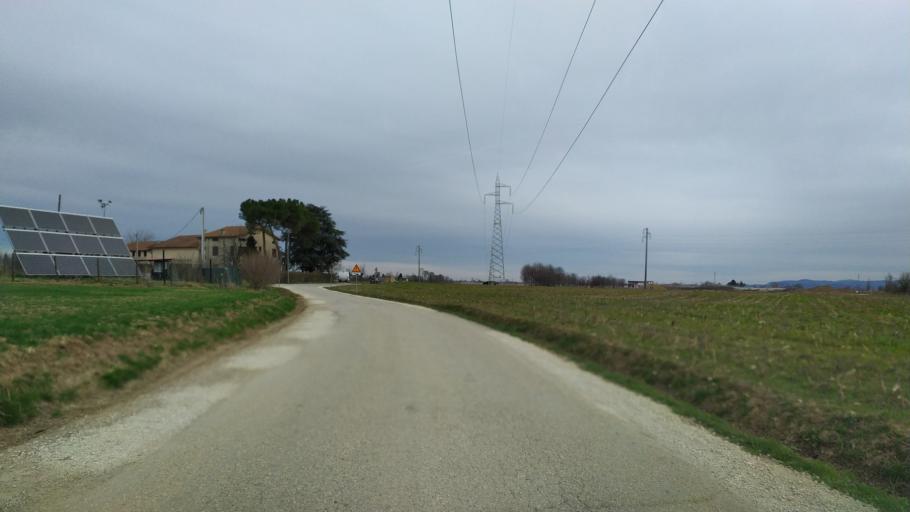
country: IT
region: Veneto
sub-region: Provincia di Vicenza
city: Malo
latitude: 45.6564
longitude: 11.4338
